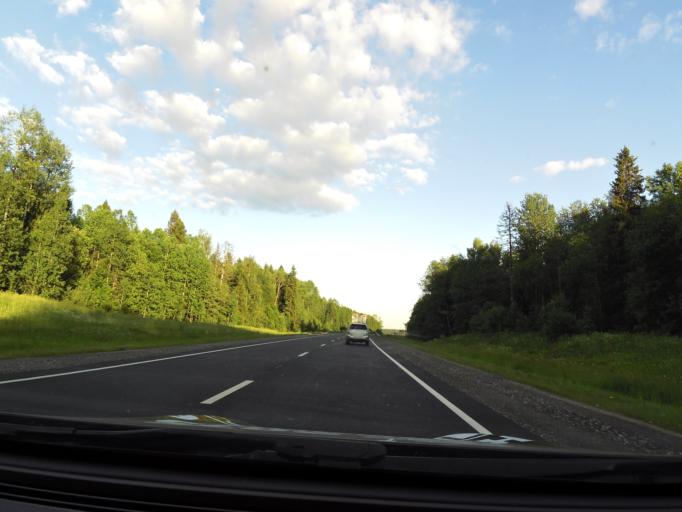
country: RU
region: Vologda
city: Gryazovets
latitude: 59.0422
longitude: 40.1022
